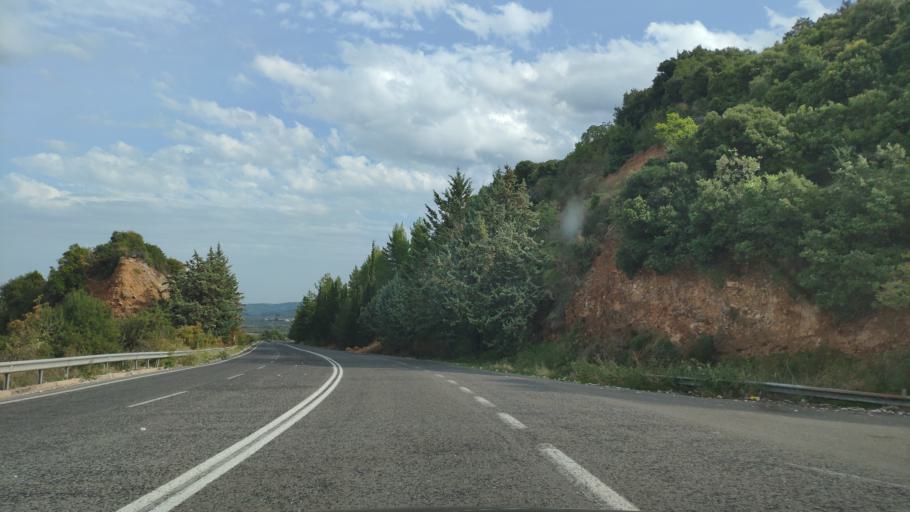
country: GR
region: Central Greece
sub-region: Nomos Fthiotidos
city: Anthili
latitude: 38.8009
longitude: 22.4983
